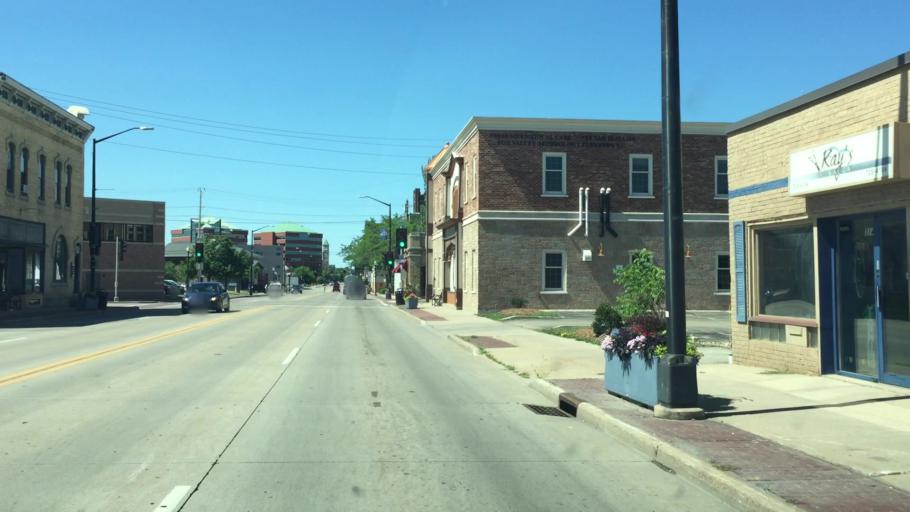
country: US
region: Wisconsin
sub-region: Winnebago County
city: Neenah
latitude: 44.1908
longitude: -88.4577
